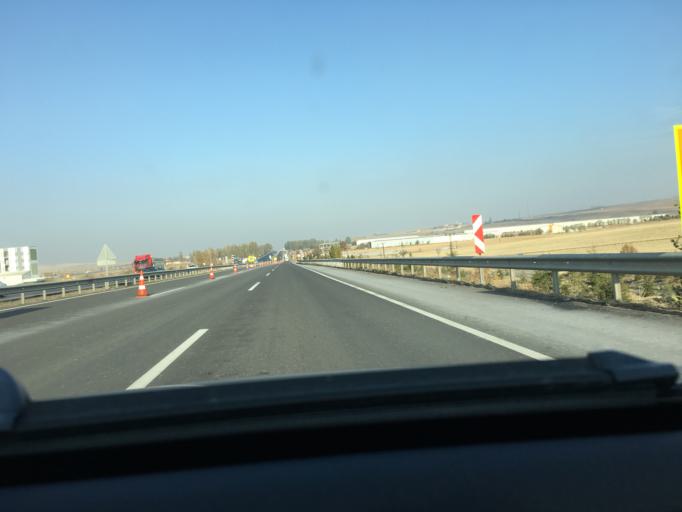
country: TR
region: Ankara
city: Temelli
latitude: 39.6817
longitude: 32.2413
